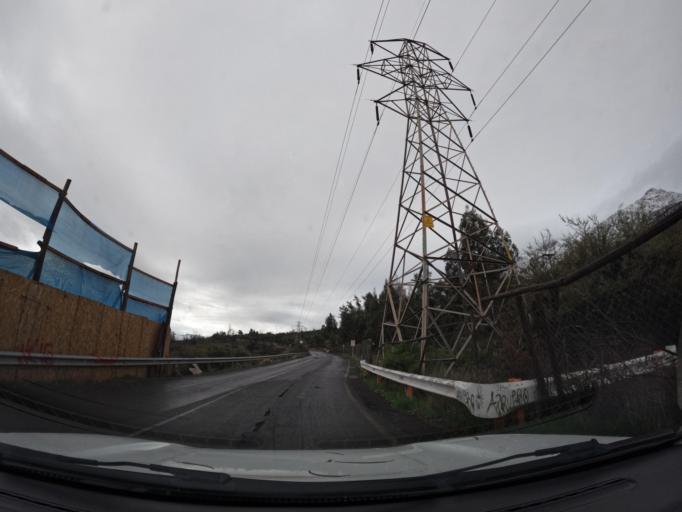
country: CL
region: Santiago Metropolitan
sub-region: Provincia de Santiago
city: Villa Presidente Frei, Nunoa, Santiago, Chile
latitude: -33.4943
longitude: -70.5187
